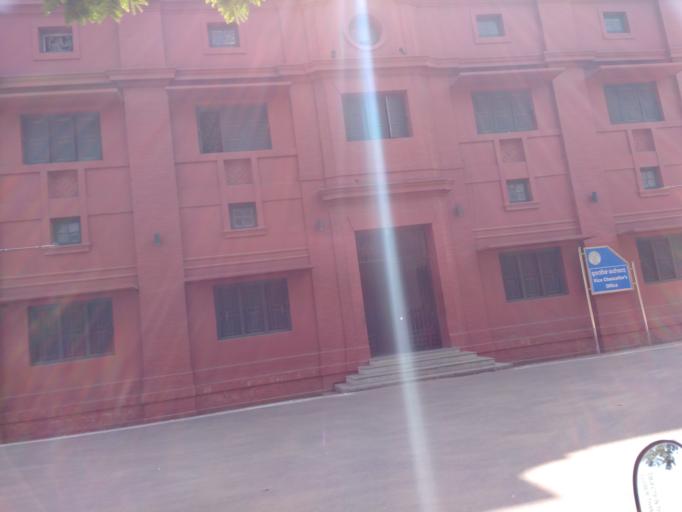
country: IN
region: Odisha
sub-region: Cuttack
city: Cuttack
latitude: 20.4660
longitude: 85.8944
